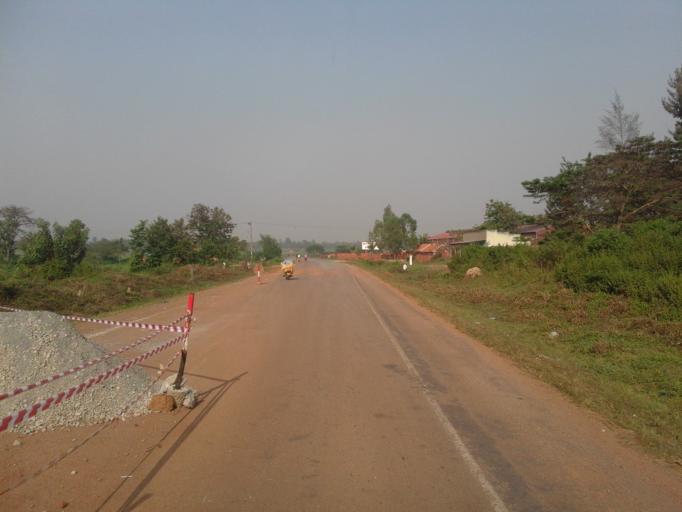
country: UG
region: Eastern Region
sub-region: Mbale District
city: Mbale
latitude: 1.0755
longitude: 34.1103
